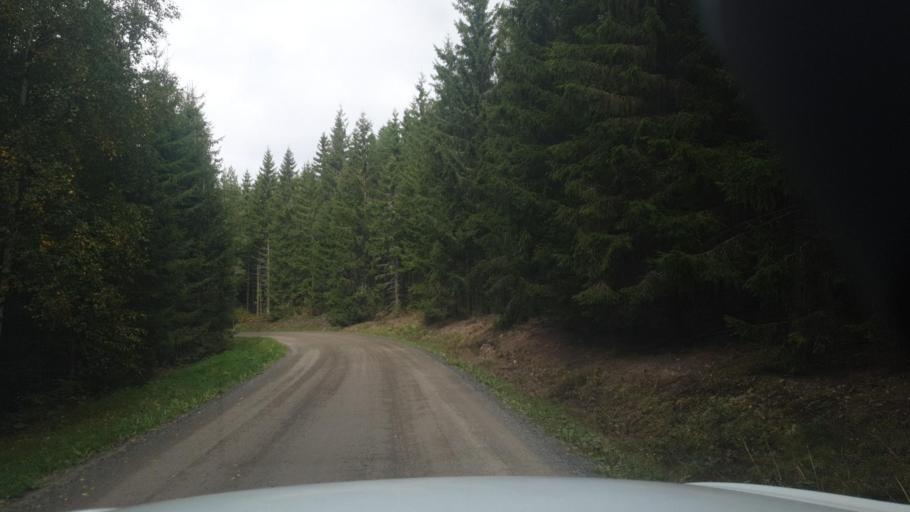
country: SE
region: Vaermland
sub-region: Sunne Kommun
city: Sunne
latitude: 59.8552
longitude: 12.9284
